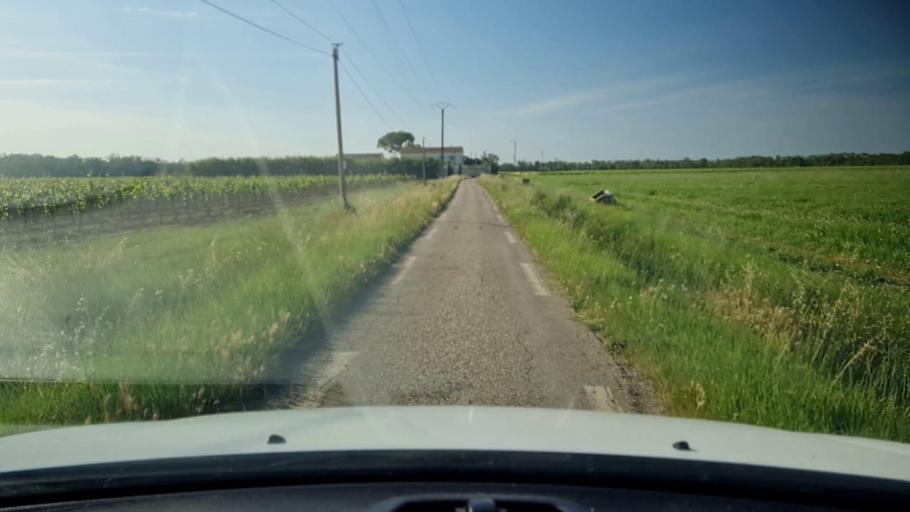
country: FR
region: Languedoc-Roussillon
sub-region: Departement du Gard
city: Le Cailar
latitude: 43.6406
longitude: 4.2294
